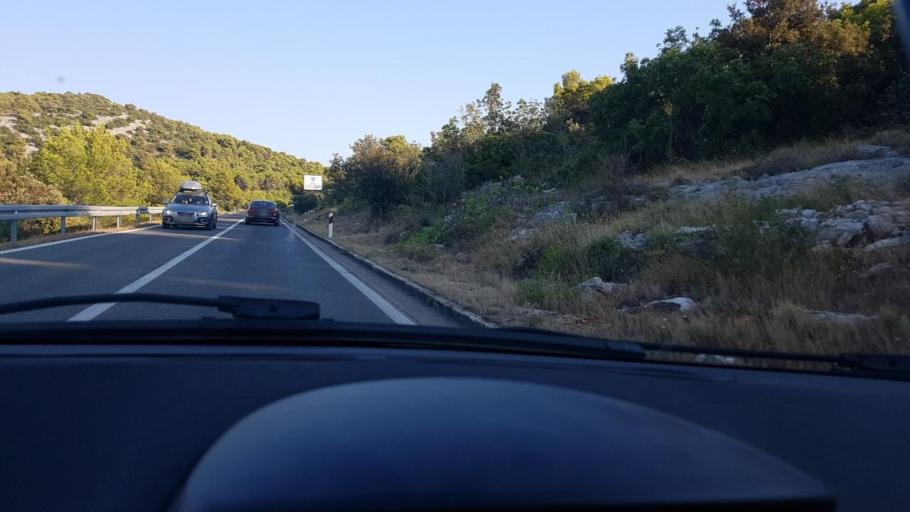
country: HR
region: Sibensko-Kniniska
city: Murter
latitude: 43.8041
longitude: 15.6101
